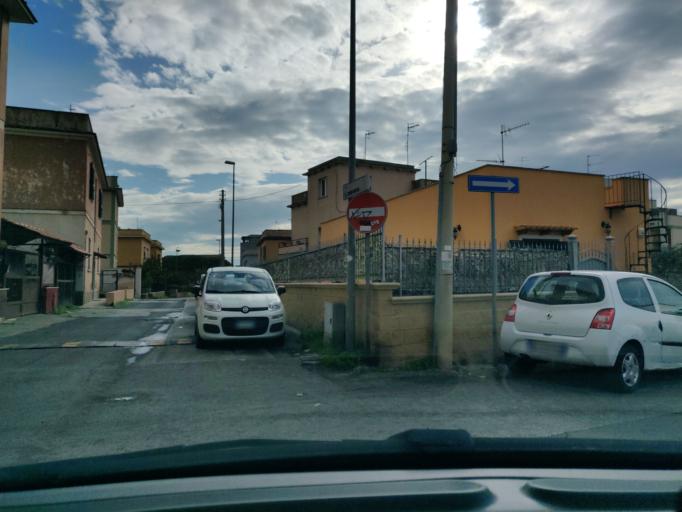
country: IT
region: Latium
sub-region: Citta metropolitana di Roma Capitale
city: Civitavecchia
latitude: 42.0923
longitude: 11.8085
